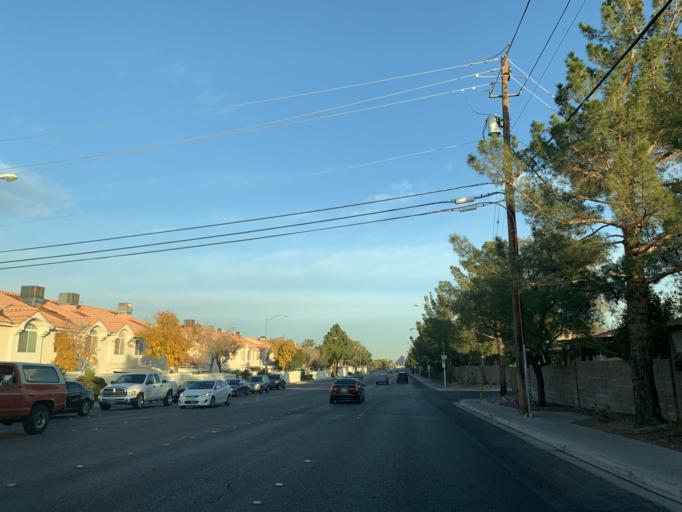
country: US
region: Nevada
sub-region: Clark County
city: Spring Valley
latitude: 36.0926
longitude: -115.2242
